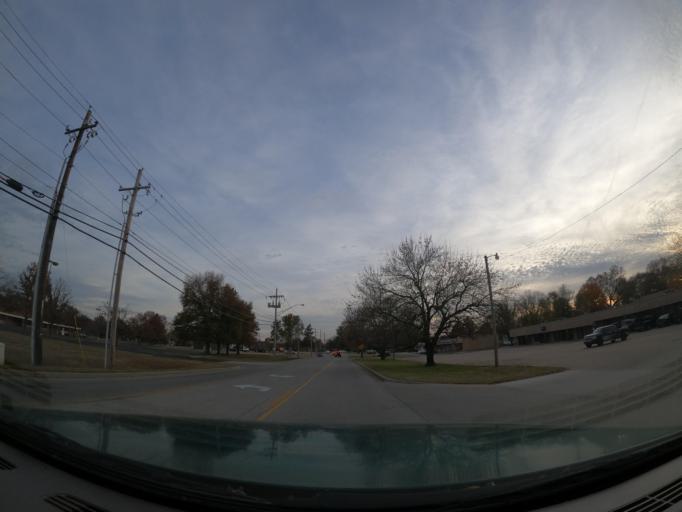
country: US
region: Oklahoma
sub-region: Tulsa County
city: Broken Arrow
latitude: 35.9755
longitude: -95.7974
